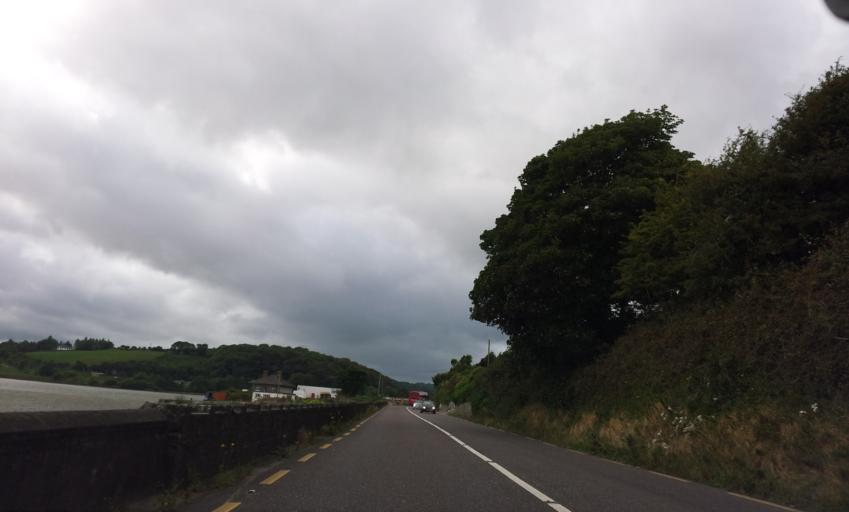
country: IE
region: Munster
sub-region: County Cork
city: Youghal
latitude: 51.9780
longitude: -7.8461
